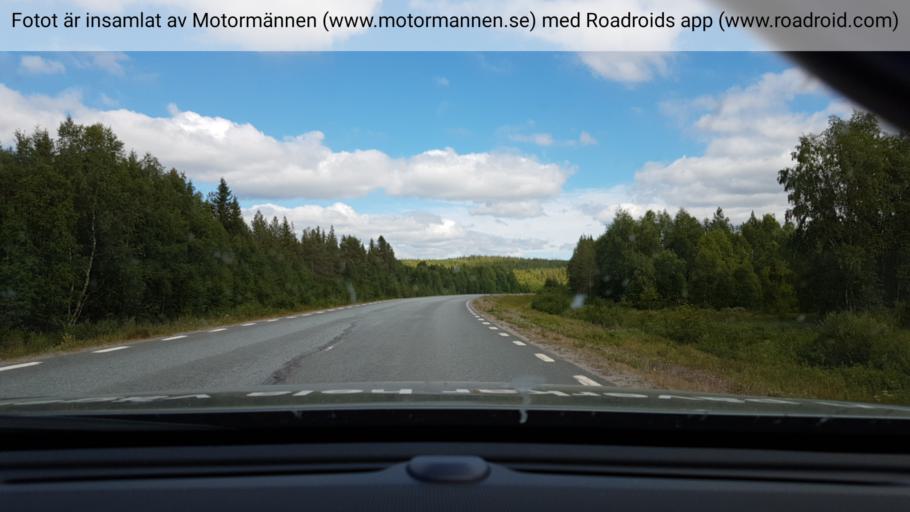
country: SE
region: Vaesterbotten
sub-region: Sorsele Kommun
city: Sorsele
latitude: 65.5390
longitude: 17.5565
